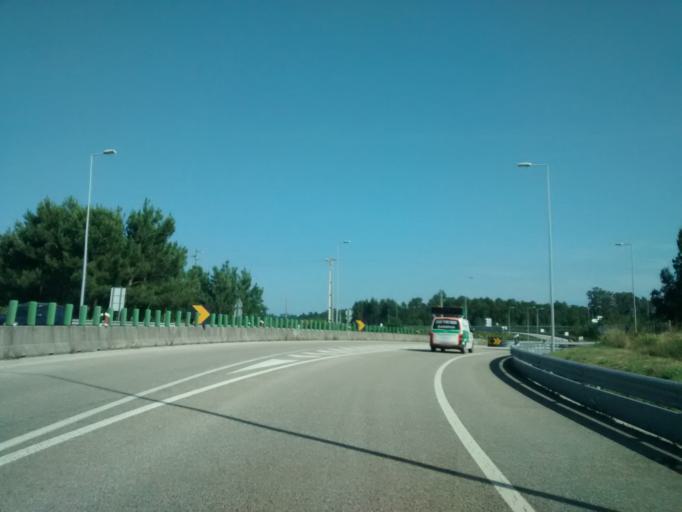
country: PT
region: Leiria
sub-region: Pombal
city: Lourical
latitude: 39.9903
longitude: -8.7888
